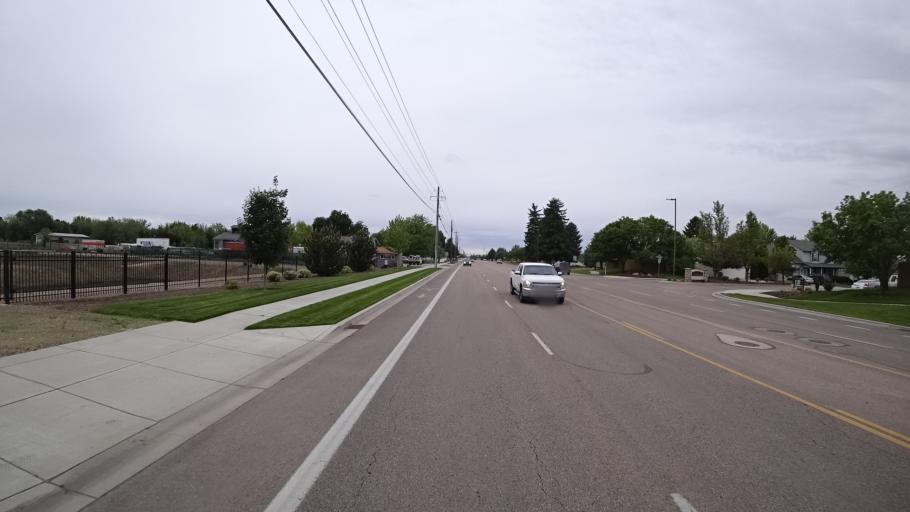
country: US
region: Idaho
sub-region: Ada County
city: Meridian
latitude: 43.6338
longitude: -116.3445
